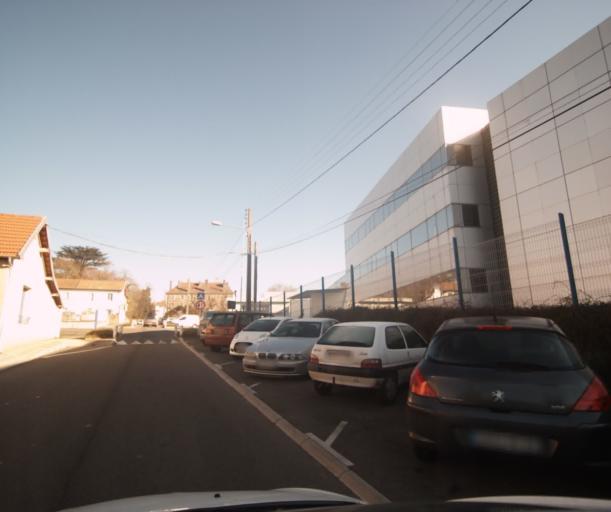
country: FR
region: Franche-Comte
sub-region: Departement du Doubs
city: Besancon
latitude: 47.2409
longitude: 5.9989
